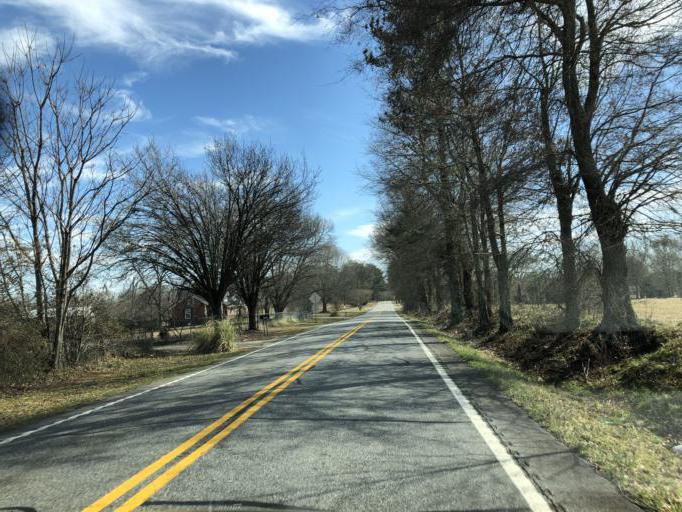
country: US
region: South Carolina
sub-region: Spartanburg County
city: Mayo
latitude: 35.0535
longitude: -81.9028
